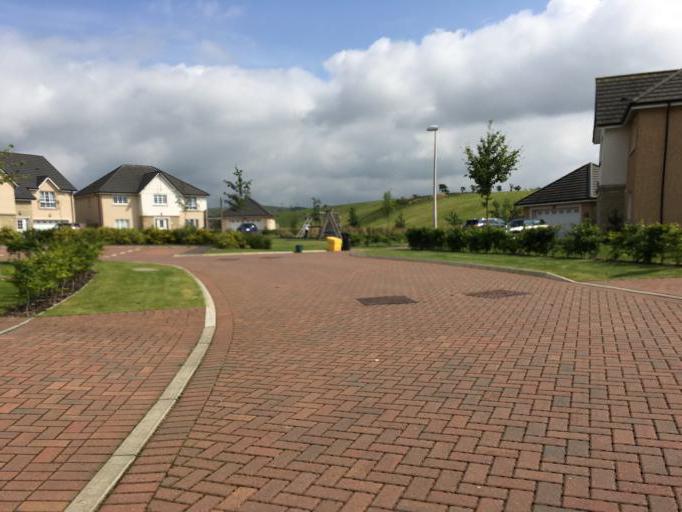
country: GB
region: Scotland
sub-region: West Lothian
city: Mid Calder
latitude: 55.8617
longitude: -3.5027
